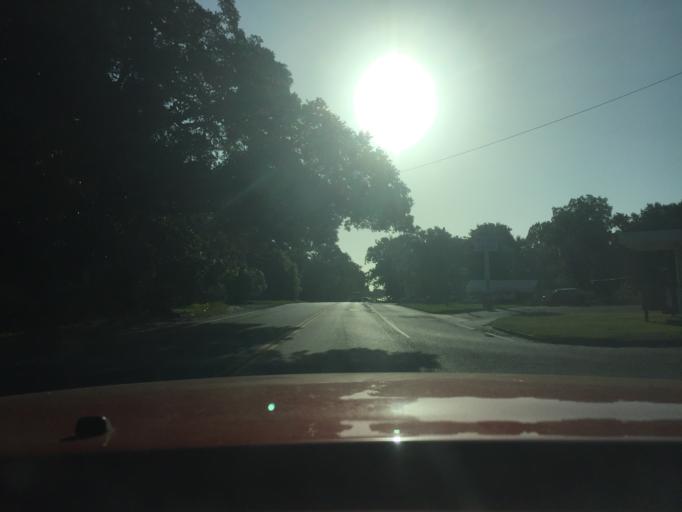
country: US
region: Georgia
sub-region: Chatham County
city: Savannah
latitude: 32.0551
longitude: -81.1367
